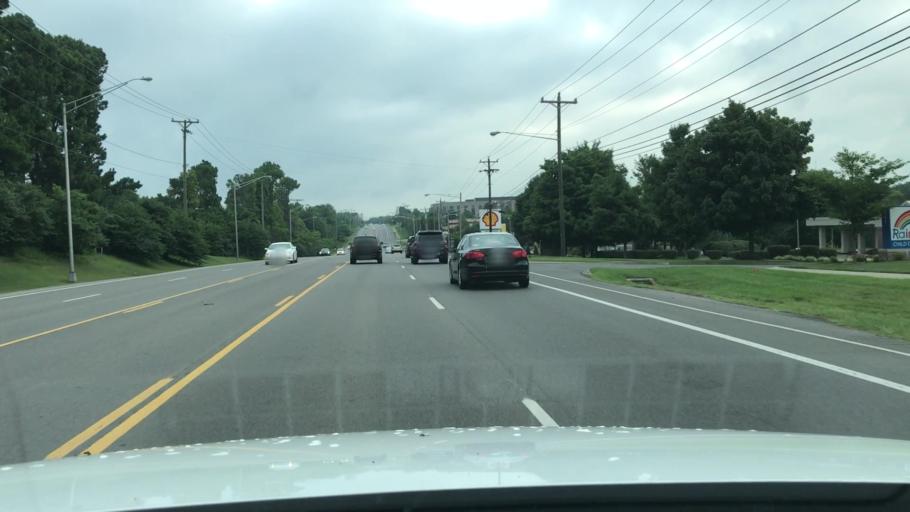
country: US
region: Tennessee
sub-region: Sumner County
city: Hendersonville
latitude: 36.3203
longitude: -86.5773
